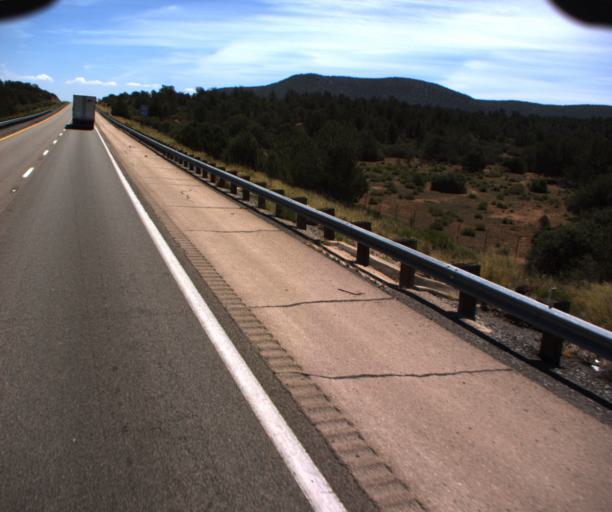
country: US
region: Arizona
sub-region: Mohave County
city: Peach Springs
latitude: 35.2075
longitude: -113.2859
